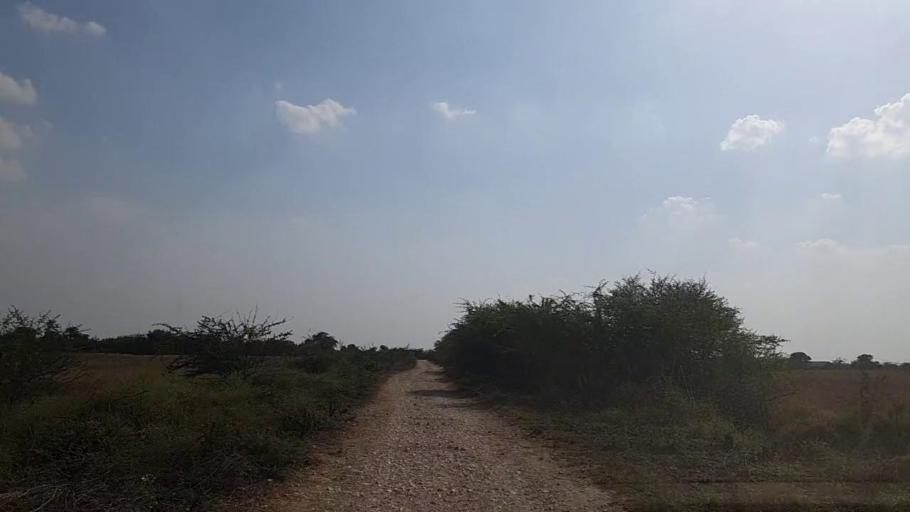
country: PK
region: Sindh
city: Jati
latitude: 24.4804
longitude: 68.3397
